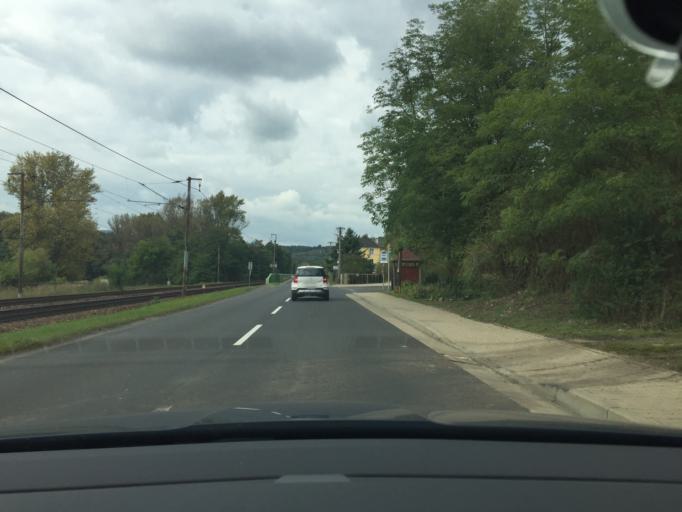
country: CZ
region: Ustecky
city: Lovosice
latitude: 50.5320
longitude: 14.0695
